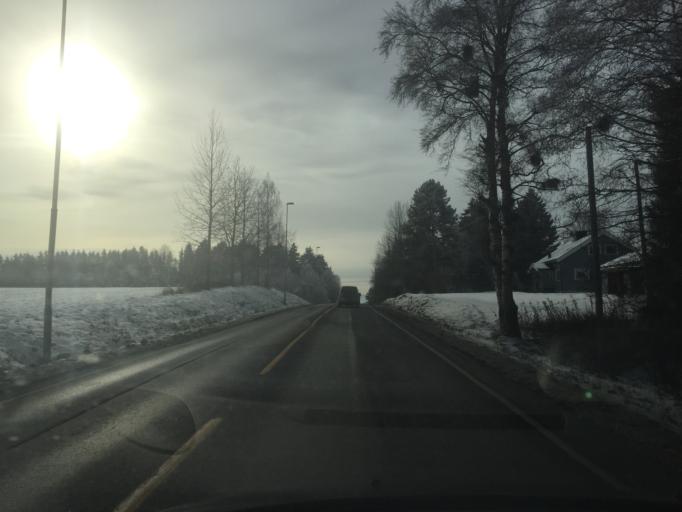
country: NO
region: Hedmark
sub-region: Loten
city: Loten
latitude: 60.8126
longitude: 11.3074
